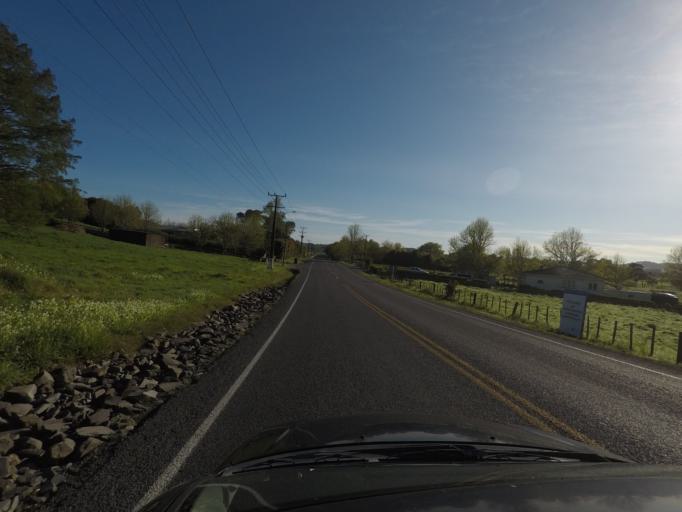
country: NZ
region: Auckland
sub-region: Auckland
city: Red Hill
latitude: -37.0122
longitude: 174.9506
